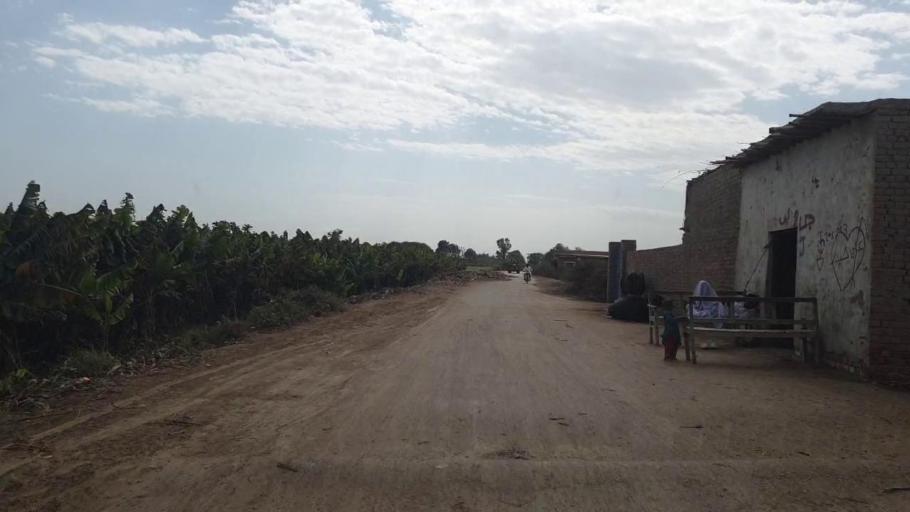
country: PK
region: Sindh
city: Hala
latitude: 25.9395
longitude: 68.4299
